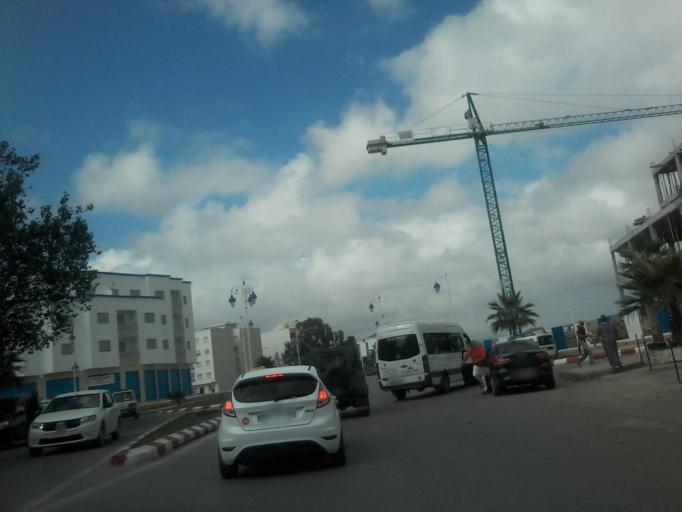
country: MA
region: Tanger-Tetouan
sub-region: Tetouan
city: Martil
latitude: 35.6275
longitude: -5.2816
